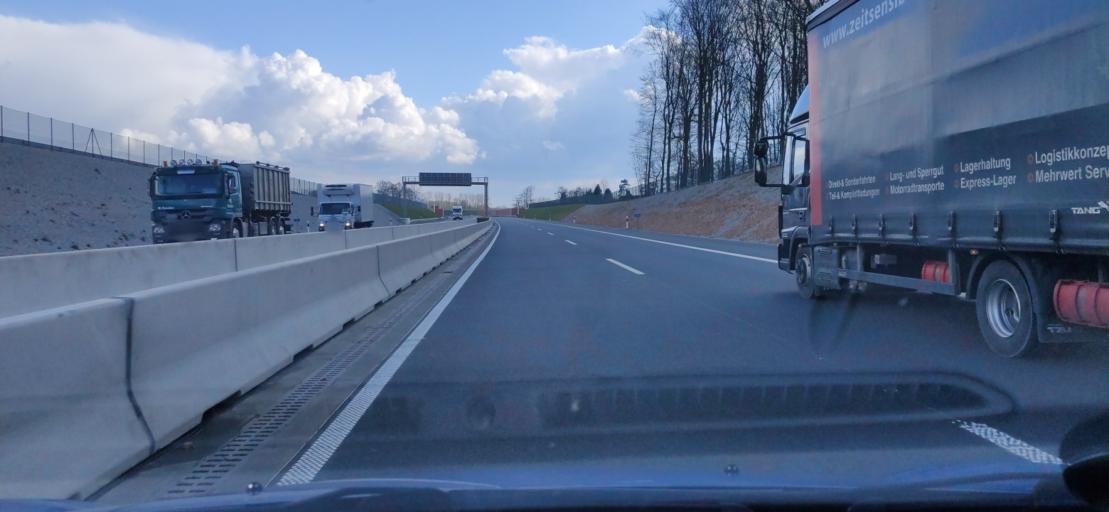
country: DE
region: North Rhine-Westphalia
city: Borgholzhausen
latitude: 52.0726
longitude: 8.2541
